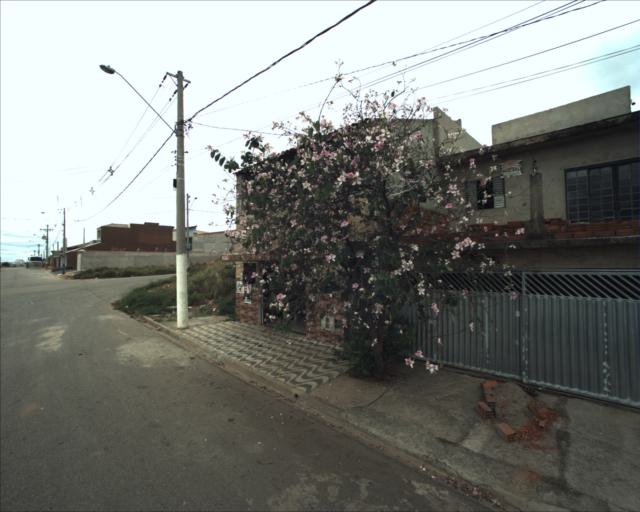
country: BR
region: Sao Paulo
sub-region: Sorocaba
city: Sorocaba
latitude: -23.4386
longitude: -47.5007
